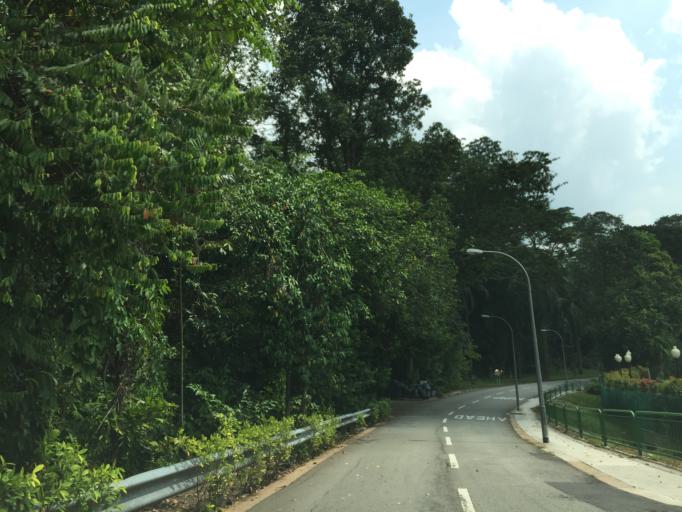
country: SG
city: Singapore
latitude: 1.3233
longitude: 103.8350
